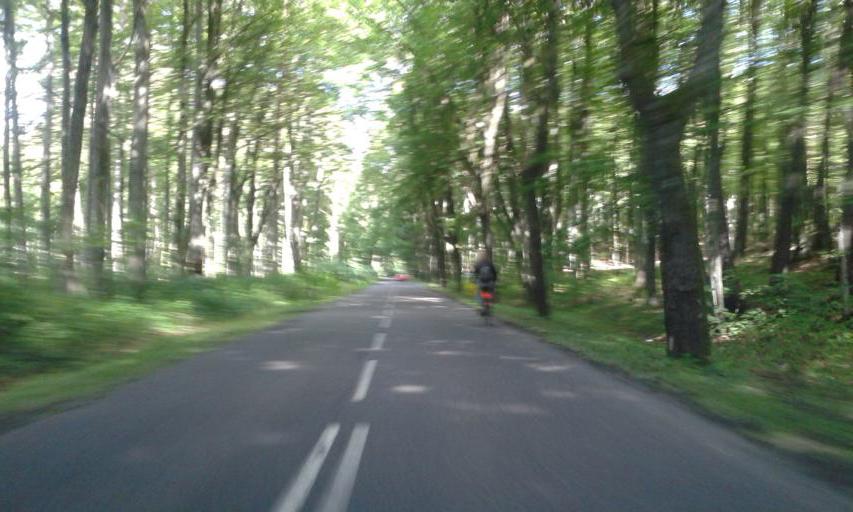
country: PL
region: West Pomeranian Voivodeship
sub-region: Powiat slawienski
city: Slawno
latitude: 54.2632
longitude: 16.6798
